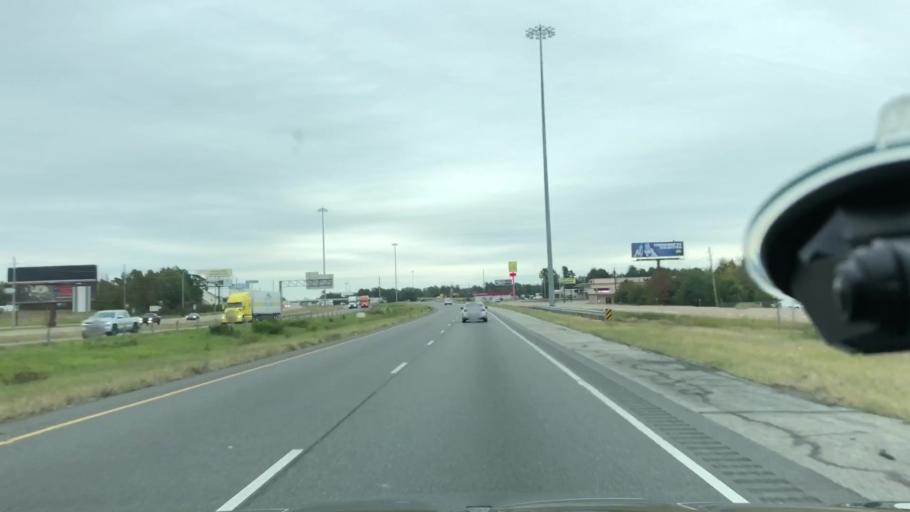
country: US
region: Arkansas
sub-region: Miller County
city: Texarkana
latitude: 33.4701
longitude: -94.0375
